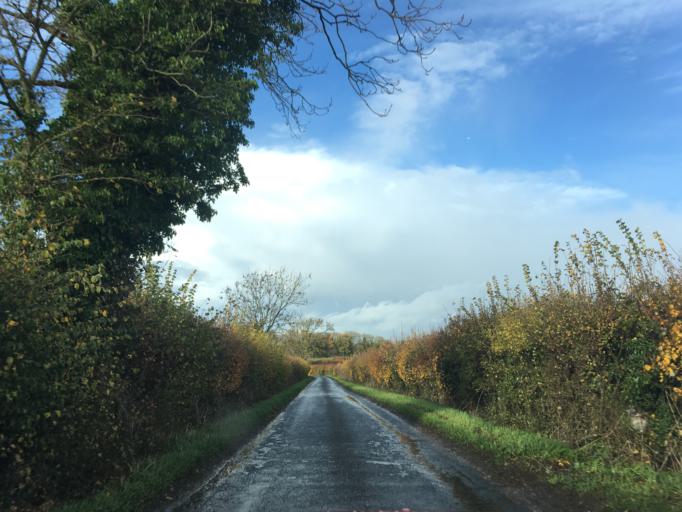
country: GB
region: England
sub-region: South Gloucestershire
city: Hinton
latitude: 51.4791
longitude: -2.4080
